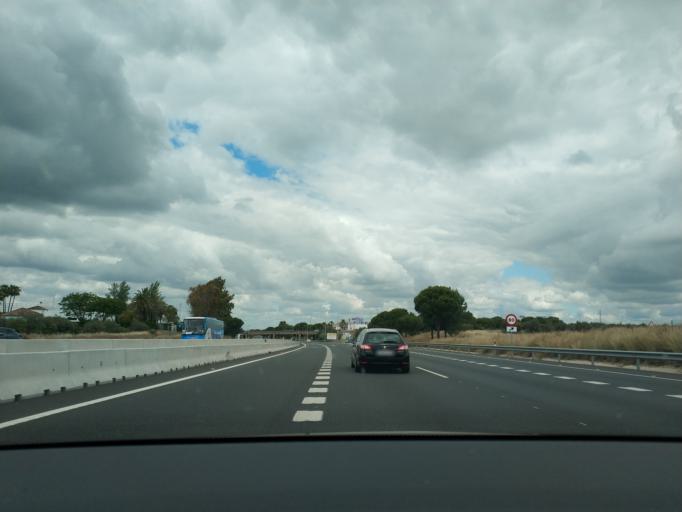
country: ES
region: Andalusia
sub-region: Provincia de Sevilla
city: Benacazon
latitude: 37.3600
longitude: -6.1962
